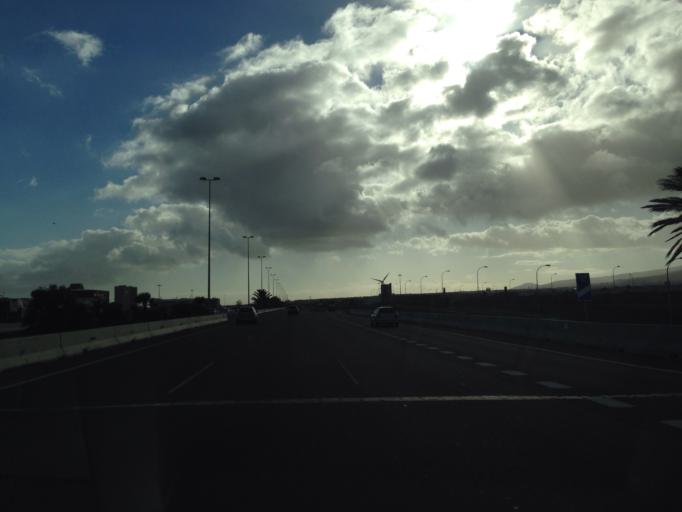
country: ES
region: Canary Islands
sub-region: Provincia de Las Palmas
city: Cruce de Arinaga
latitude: 27.8711
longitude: -15.4187
